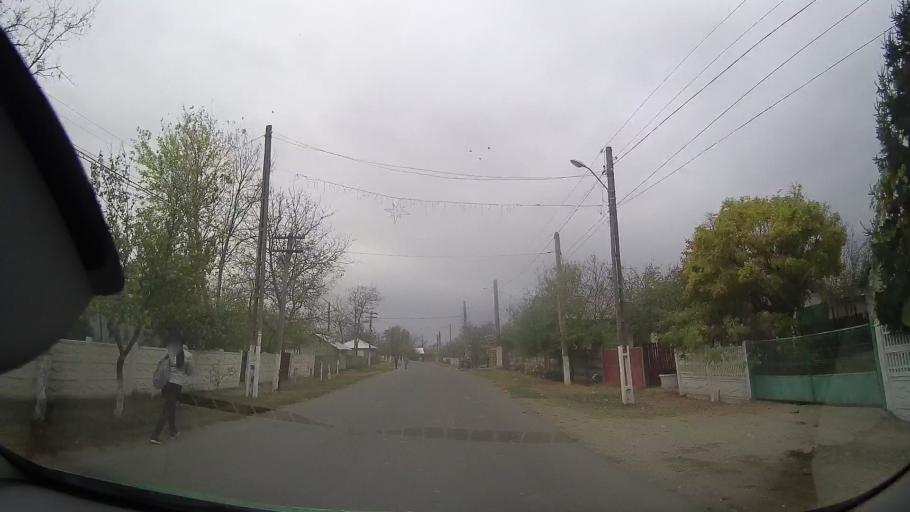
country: RO
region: Braila
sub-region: Comuna Ulmu
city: Jugureanu
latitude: 44.9433
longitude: 27.2765
